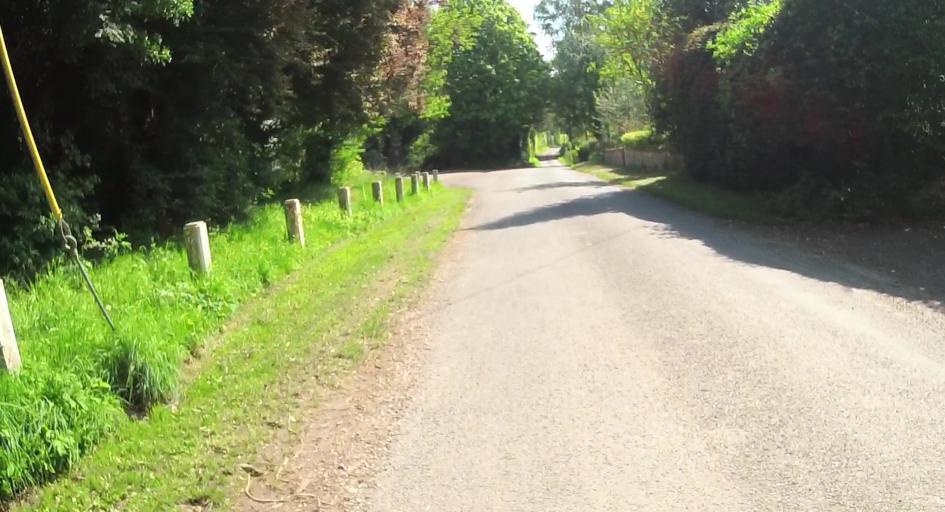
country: GB
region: England
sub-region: Hampshire
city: Kings Worthy
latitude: 51.1668
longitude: -1.3303
